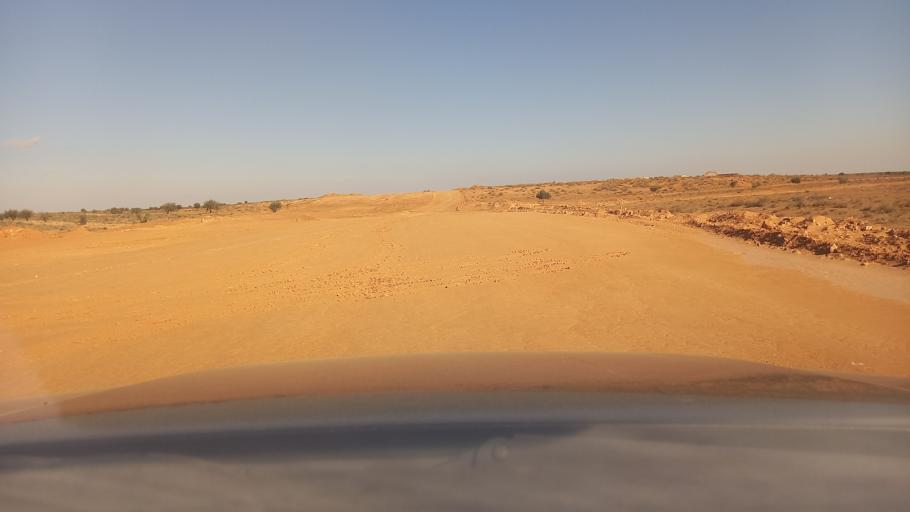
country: TN
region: Madanin
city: Medenine
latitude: 33.1718
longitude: 10.5267
